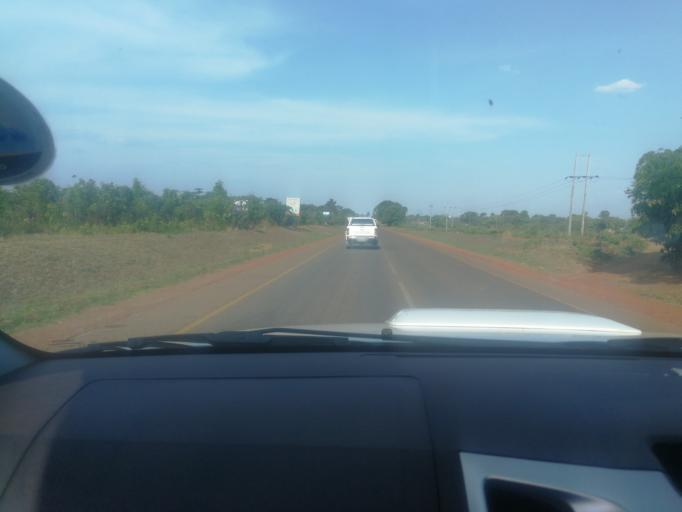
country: ZM
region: Northern
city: Kasama
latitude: -10.2181
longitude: 31.1425
